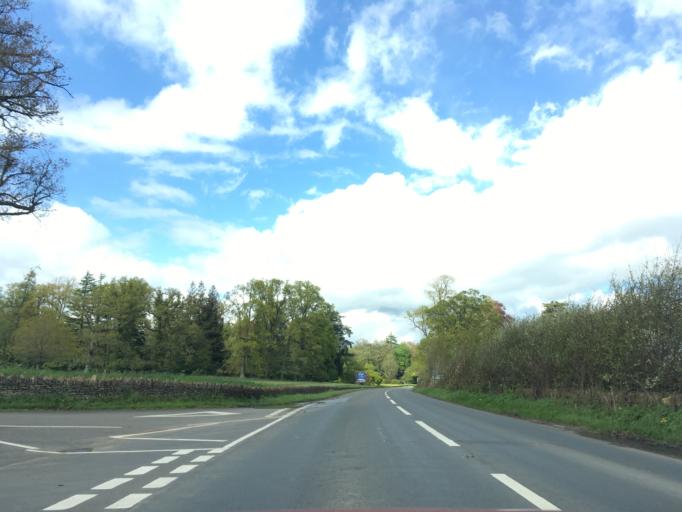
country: GB
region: England
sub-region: Gloucestershire
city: Tetbury
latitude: 51.6059
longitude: -2.2090
